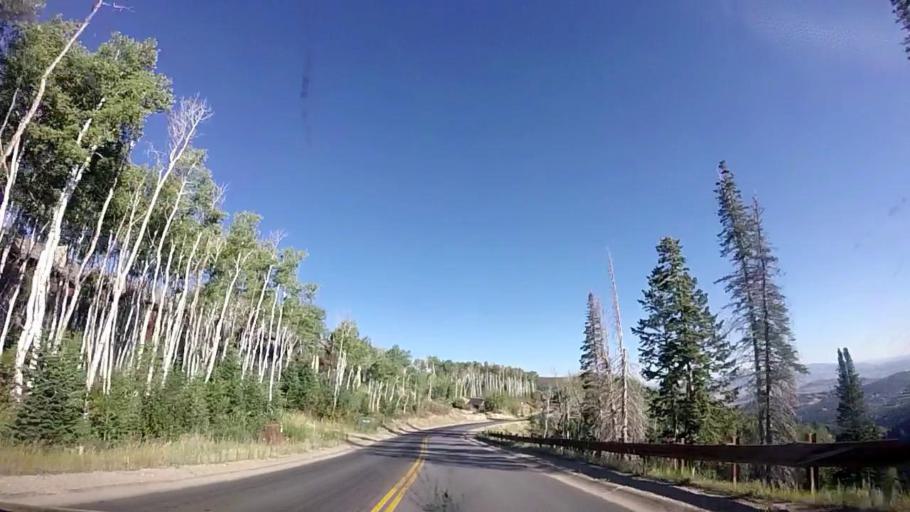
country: US
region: Utah
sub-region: Summit County
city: Park City
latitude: 40.6225
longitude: -111.4980
